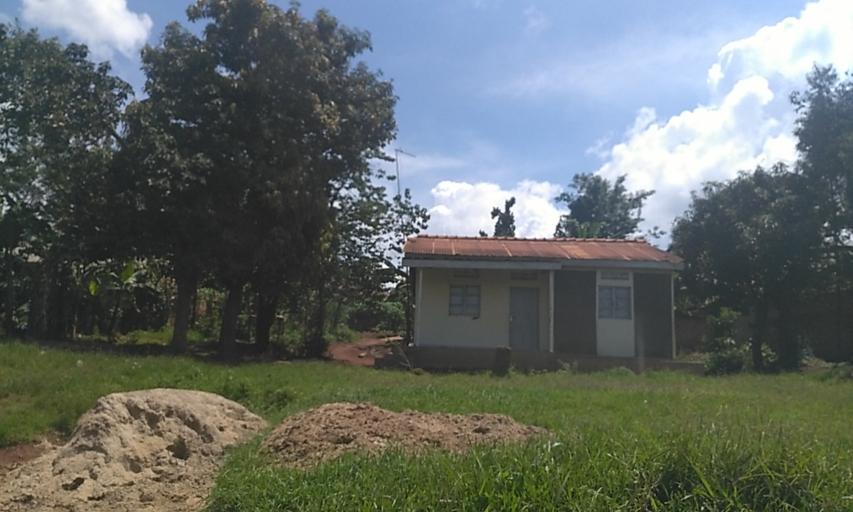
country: UG
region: Central Region
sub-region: Wakiso District
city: Wakiso
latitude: 0.4074
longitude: 32.4721
